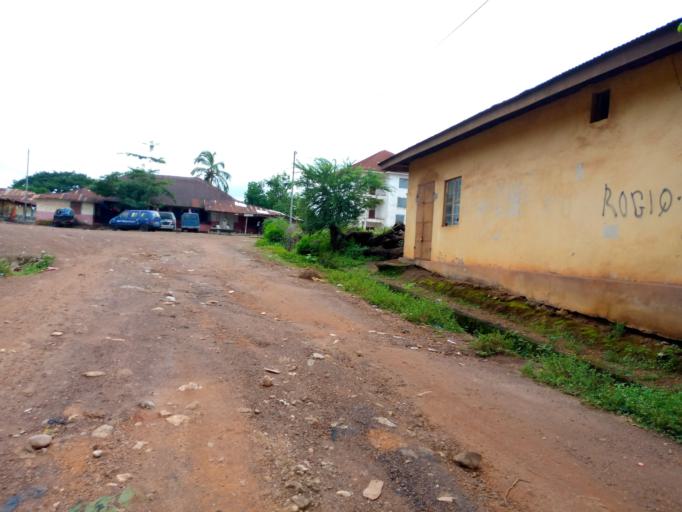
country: SL
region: Northern Province
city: Magburaka
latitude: 8.7223
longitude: -11.9449
